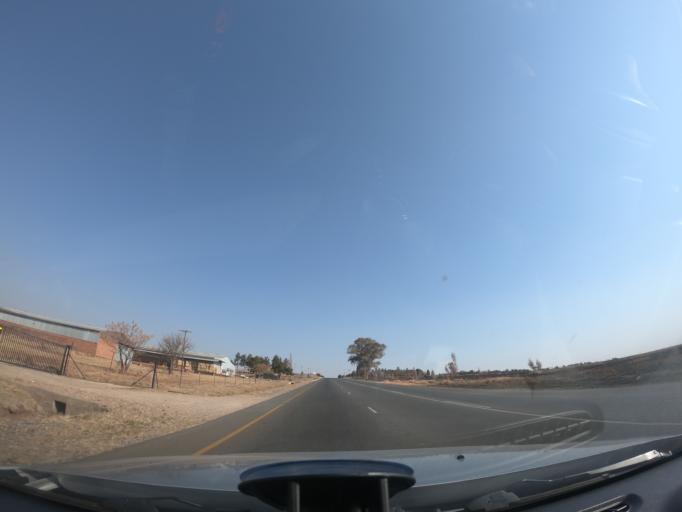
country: ZA
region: Gauteng
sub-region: City of Johannesburg Metropolitan Municipality
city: Diepsloot
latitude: -25.8639
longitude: 28.0331
